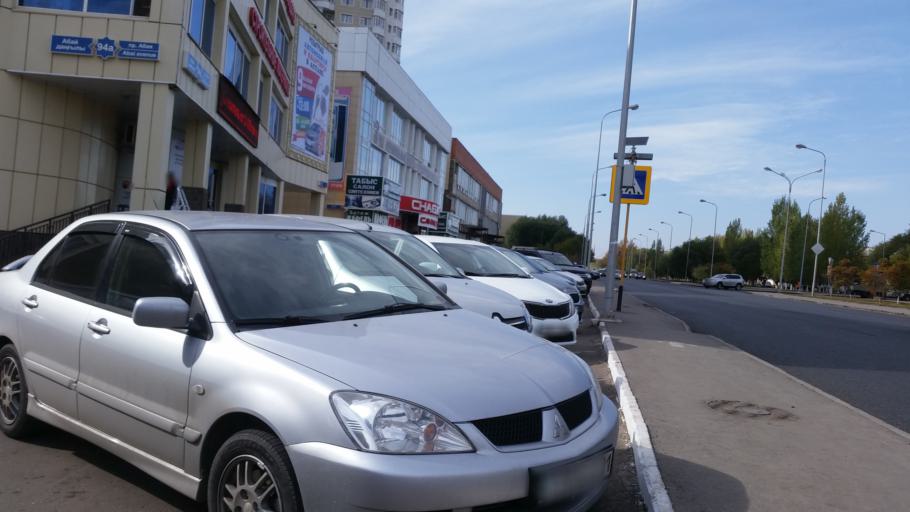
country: KZ
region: Astana Qalasy
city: Astana
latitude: 51.1641
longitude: 71.4693
